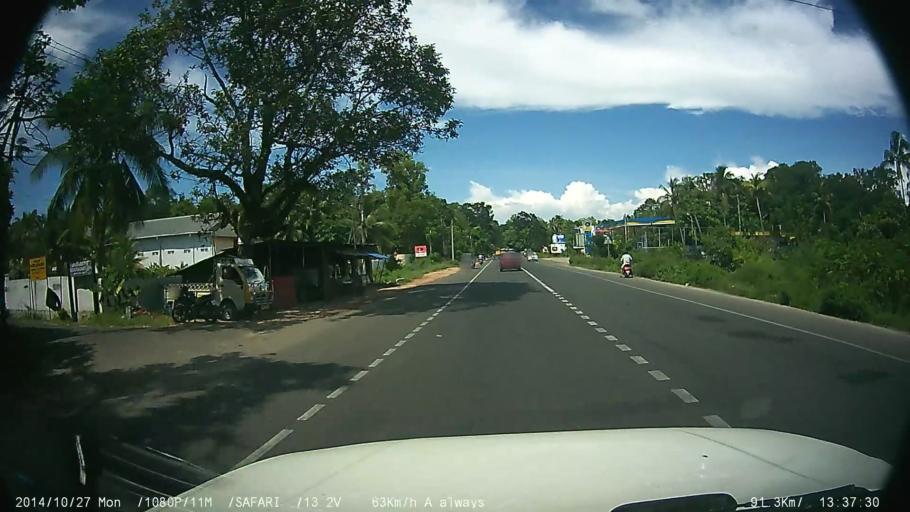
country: IN
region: Kerala
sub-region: Alappuzha
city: Shertallai
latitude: 9.6112
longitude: 76.3300
